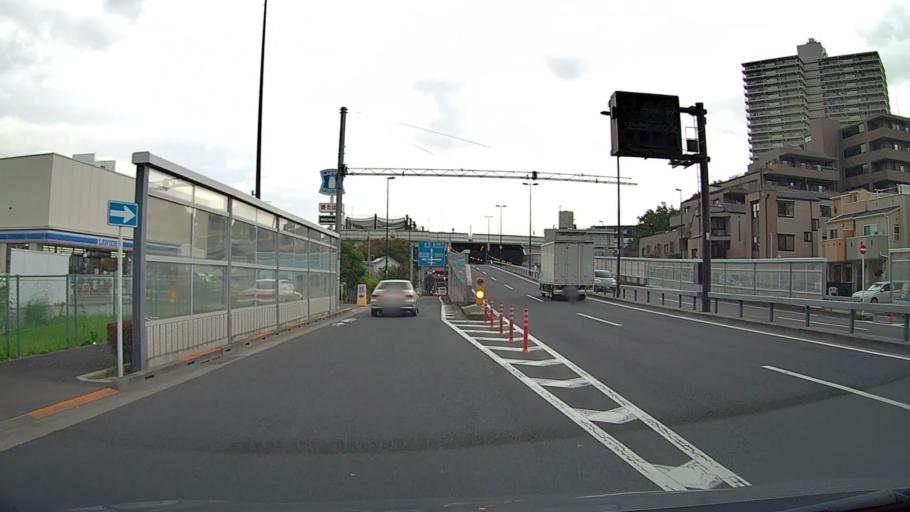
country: JP
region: Saitama
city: Shimotoda
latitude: 35.7748
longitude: 139.6751
